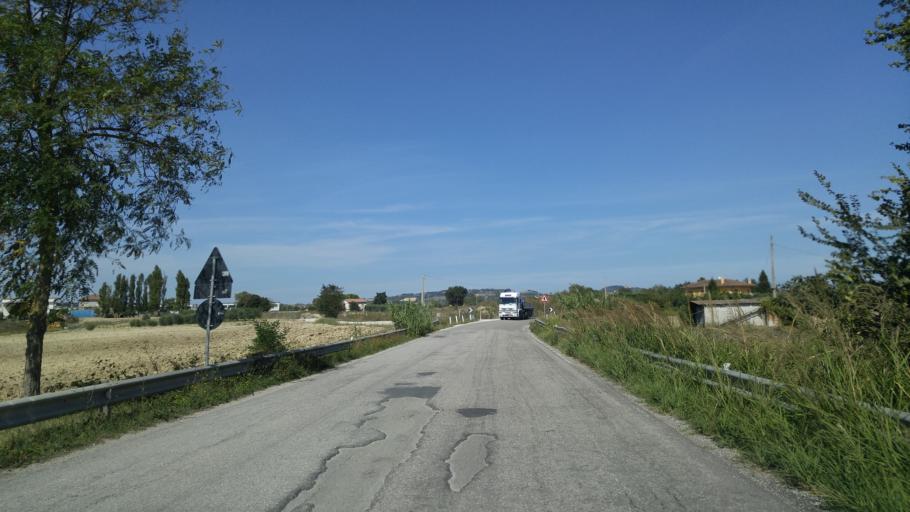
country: IT
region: The Marches
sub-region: Provincia di Pesaro e Urbino
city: Lucrezia
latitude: 43.7641
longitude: 12.9673
